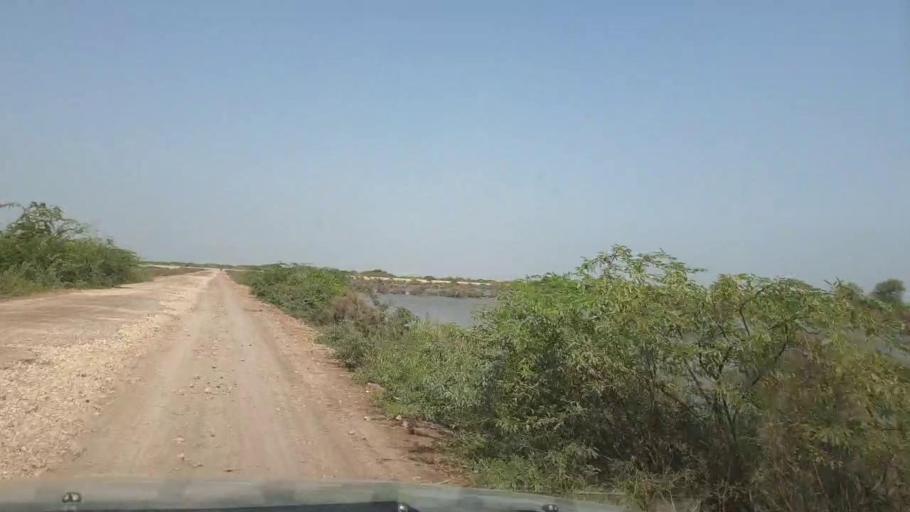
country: PK
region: Sindh
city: Tando Ghulam Ali
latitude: 25.1116
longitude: 68.8021
